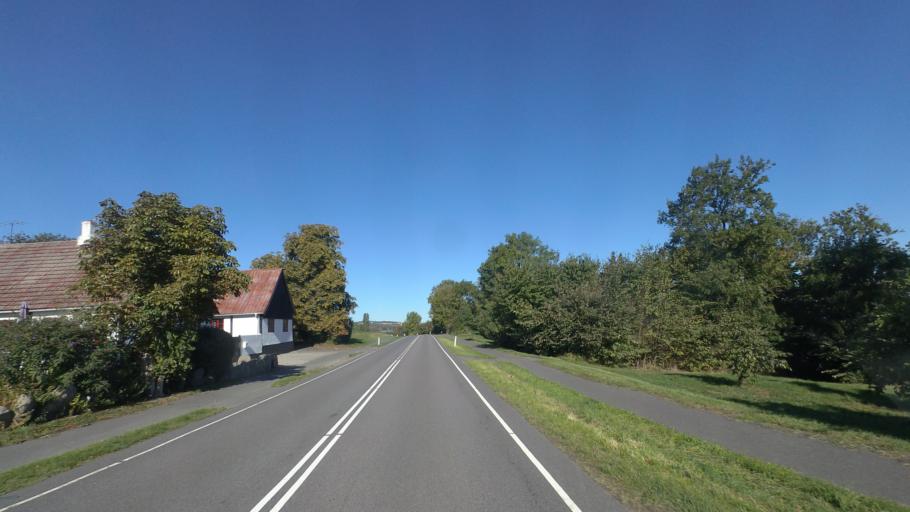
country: DK
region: Capital Region
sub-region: Bornholm Kommune
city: Akirkeby
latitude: 55.1855
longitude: 15.0056
